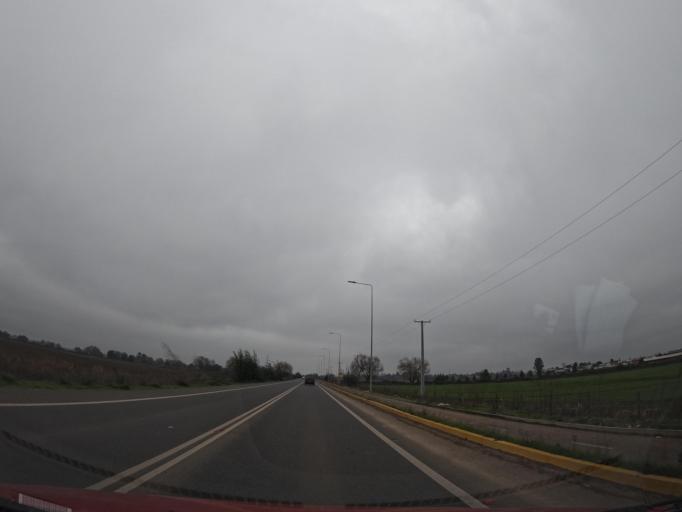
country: CL
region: Maule
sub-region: Provincia de Talca
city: San Clemente
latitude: -35.5350
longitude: -71.4736
